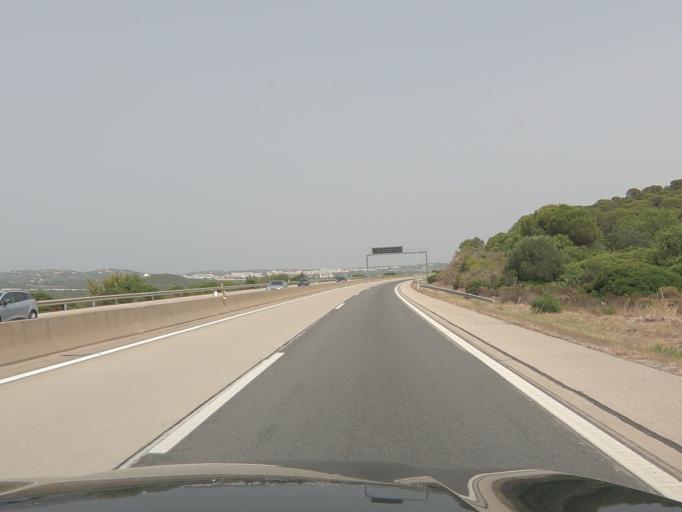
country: PT
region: Faro
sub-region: Loule
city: Vilamoura
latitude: 37.1241
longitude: -8.0748
